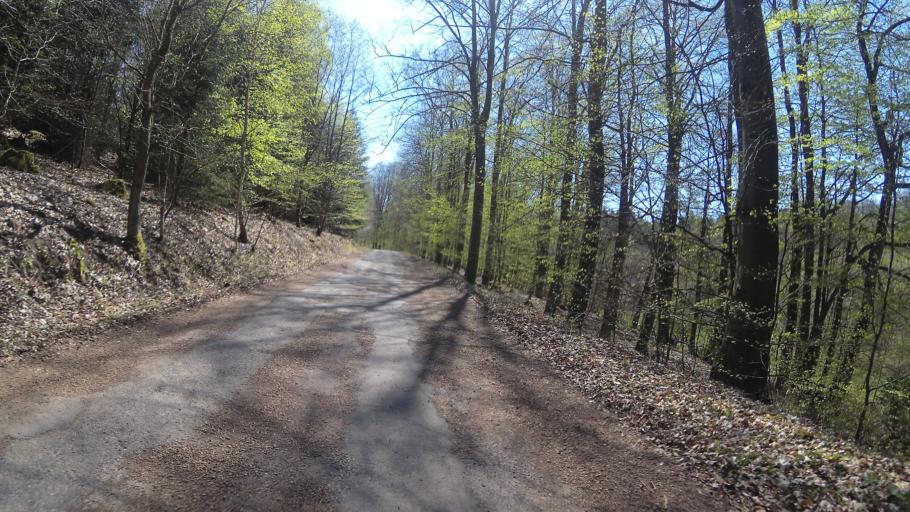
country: DE
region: Rheinland-Pfalz
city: Breitenbach
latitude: 49.4104
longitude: 7.2787
